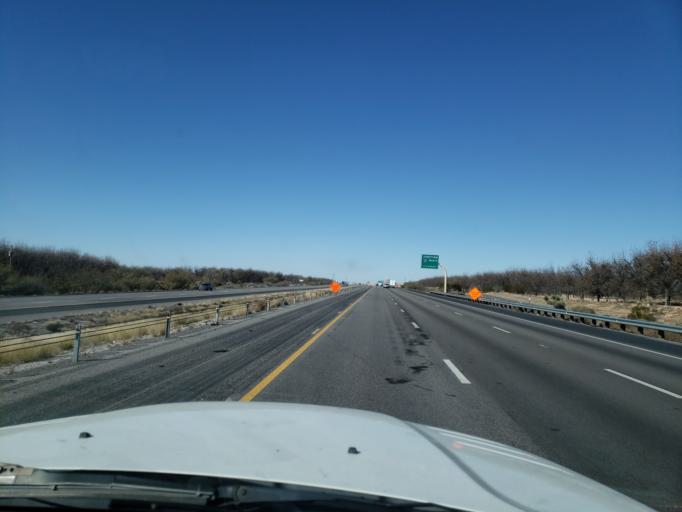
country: US
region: New Mexico
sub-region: Dona Ana County
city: University Park
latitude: 32.2353
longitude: -106.7138
